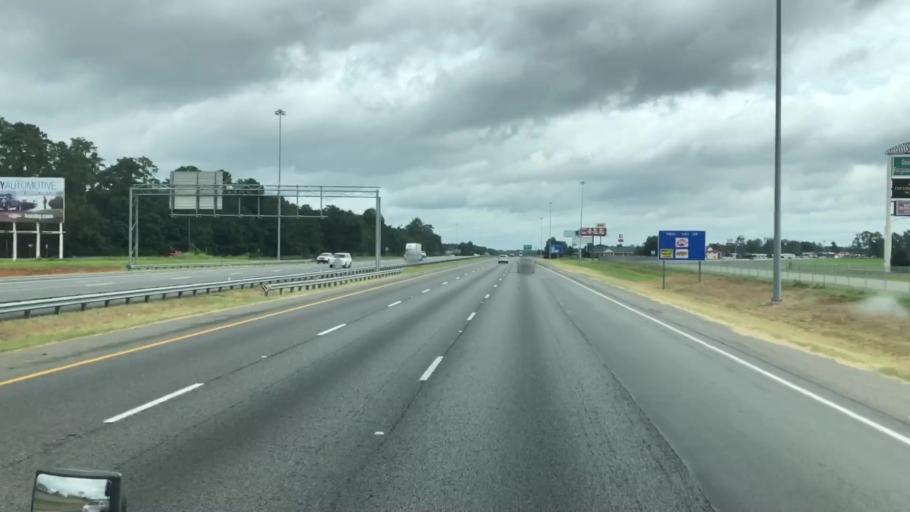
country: US
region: Georgia
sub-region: Houston County
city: Perry
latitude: 32.4387
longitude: -83.7558
